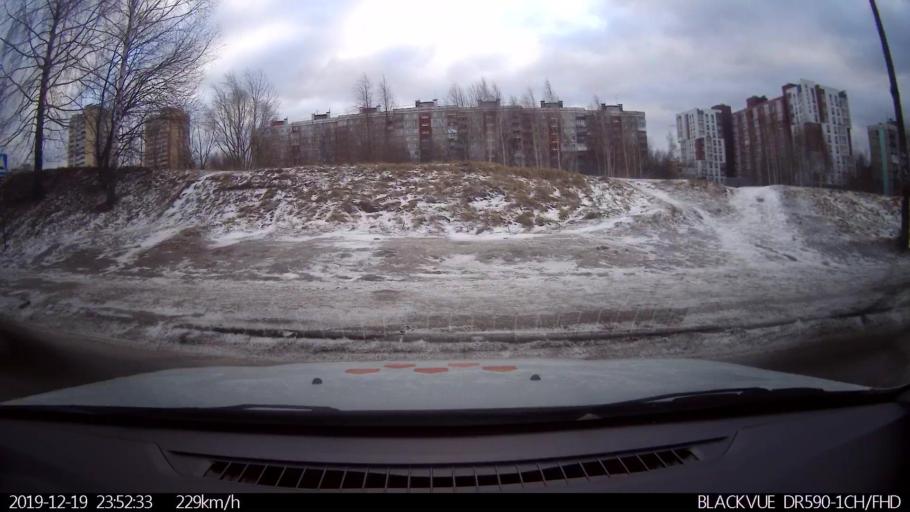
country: RU
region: Vologda
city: Molochnoye
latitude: 58.9860
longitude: 39.4900
